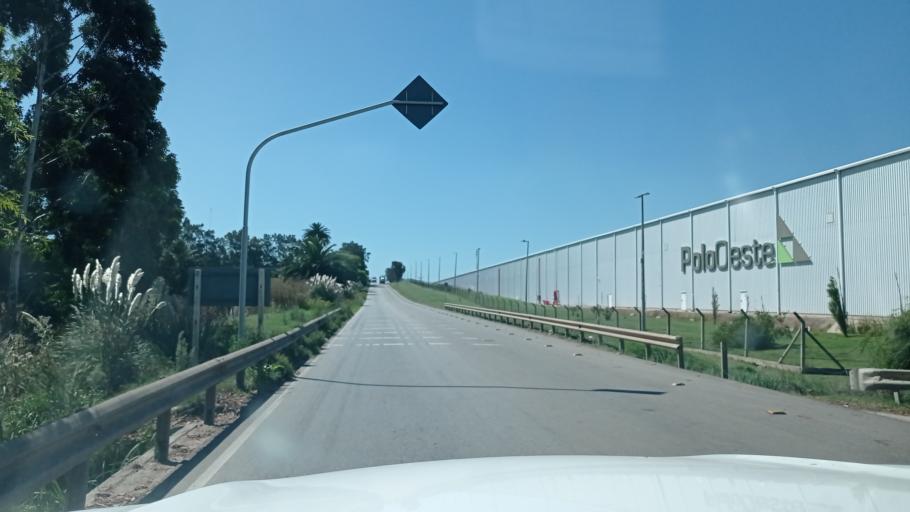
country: UY
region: Montevideo
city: Pajas Blancas
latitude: -34.8588
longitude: -56.2890
